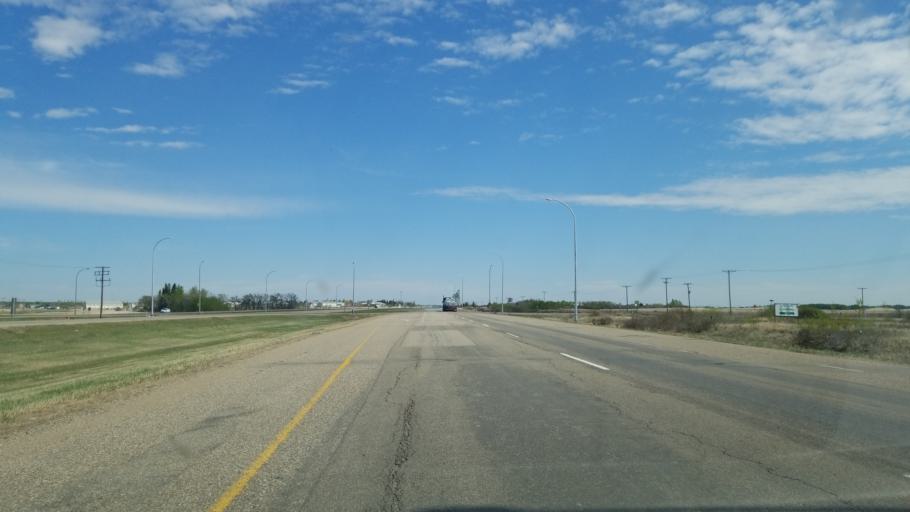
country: CA
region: Saskatchewan
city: Lloydminster
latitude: 53.1334
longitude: -109.6393
